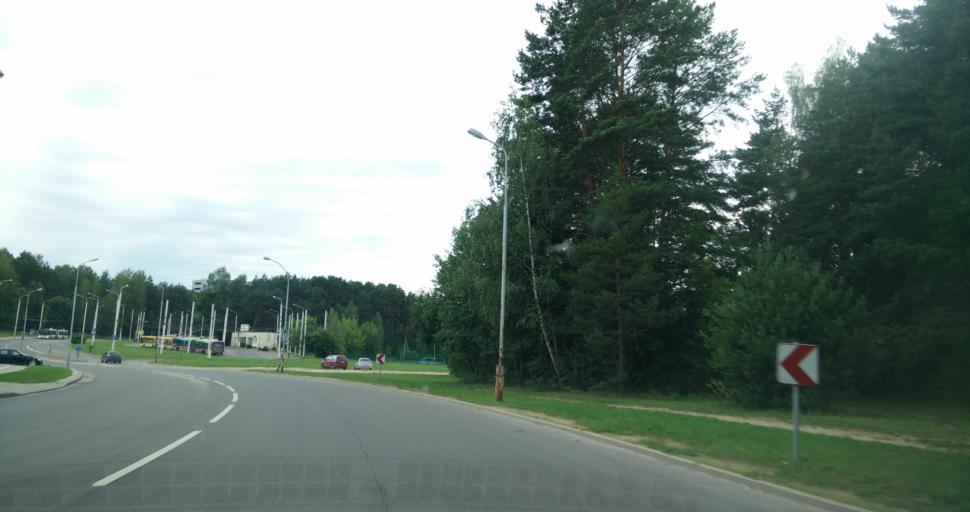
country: LT
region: Vilnius County
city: Rasos
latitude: 54.7264
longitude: 25.3431
